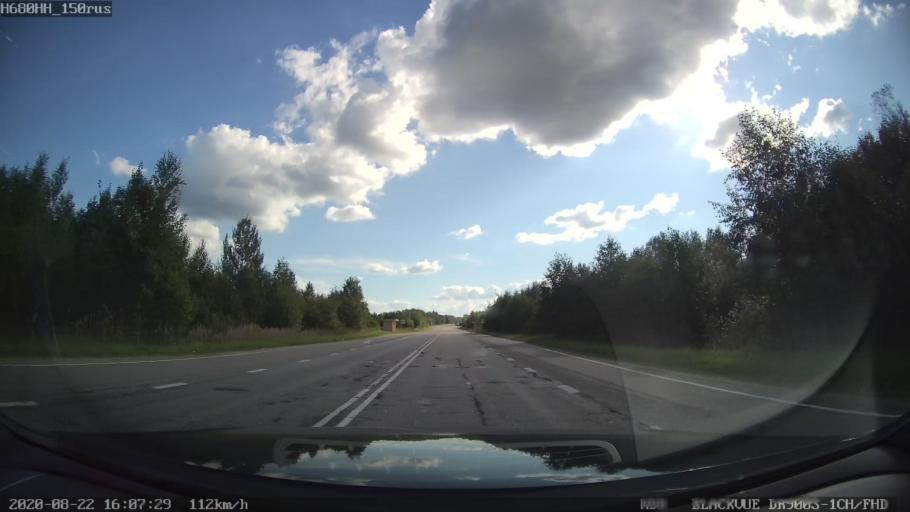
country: RU
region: Tverskaya
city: Rameshki
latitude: 57.5521
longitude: 36.3126
